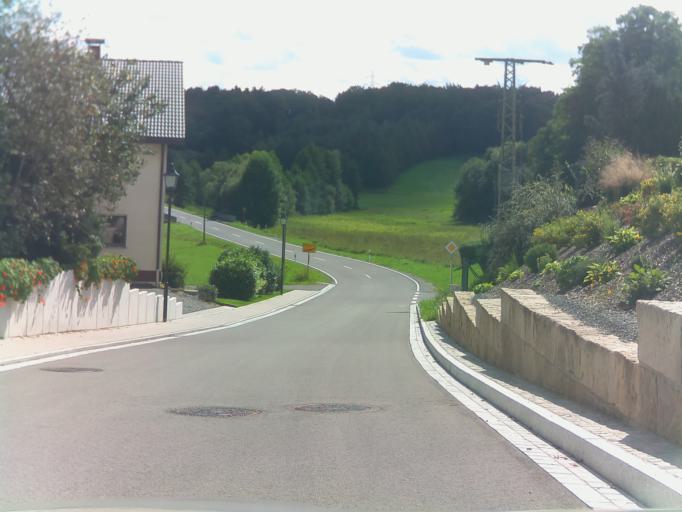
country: DE
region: Bavaria
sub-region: Regierungsbezirk Unterfranken
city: Kirchlauter
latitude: 50.0224
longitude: 10.7318
